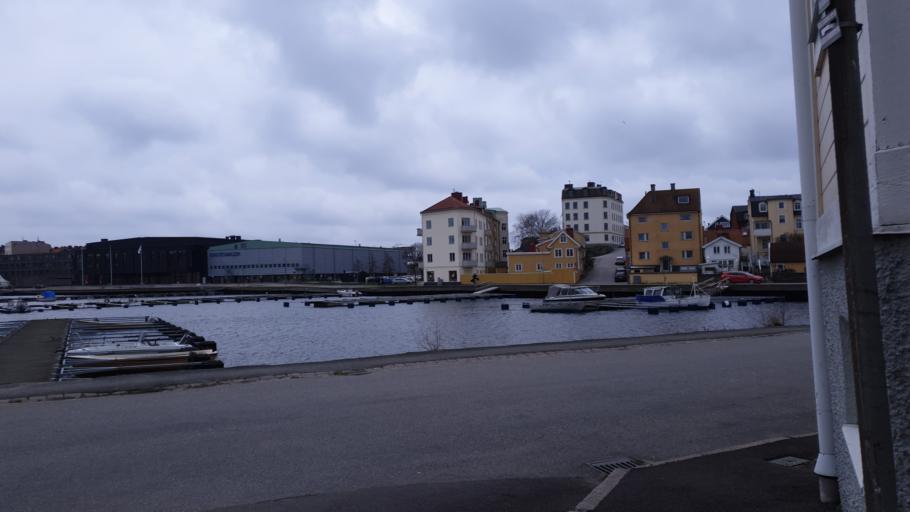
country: SE
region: Blekinge
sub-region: Karlskrona Kommun
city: Karlskrona
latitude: 56.1645
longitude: 15.5737
